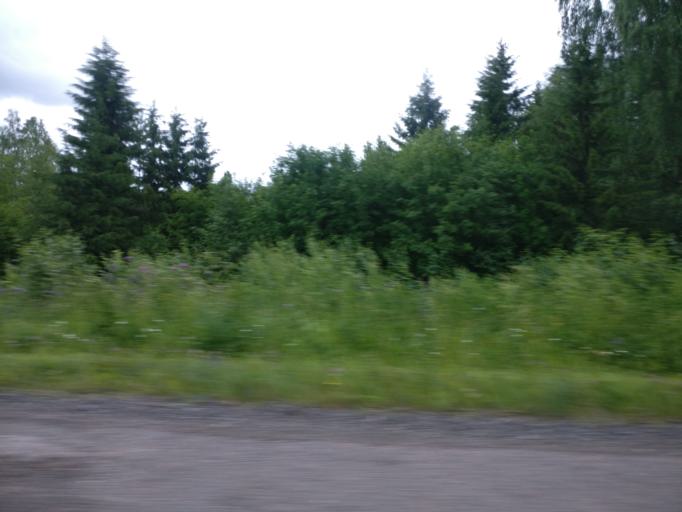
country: FI
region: Northern Savo
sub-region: Varkaus
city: Leppaevirta
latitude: 62.4358
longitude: 27.8098
